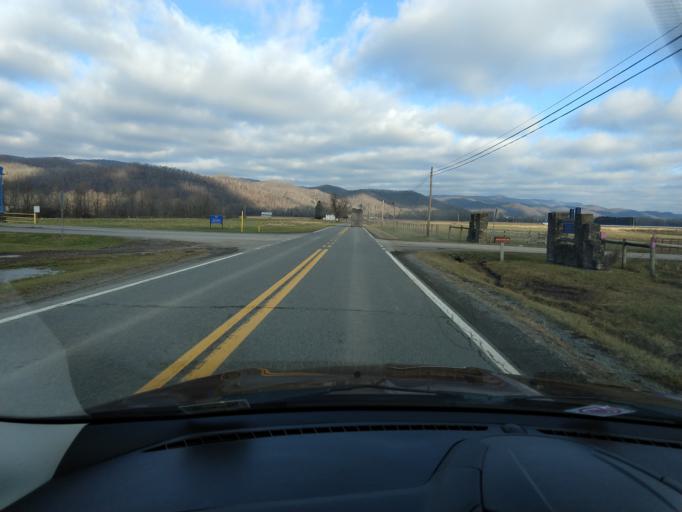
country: US
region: West Virginia
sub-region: Randolph County
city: Elkins
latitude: 38.6942
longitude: -79.9745
